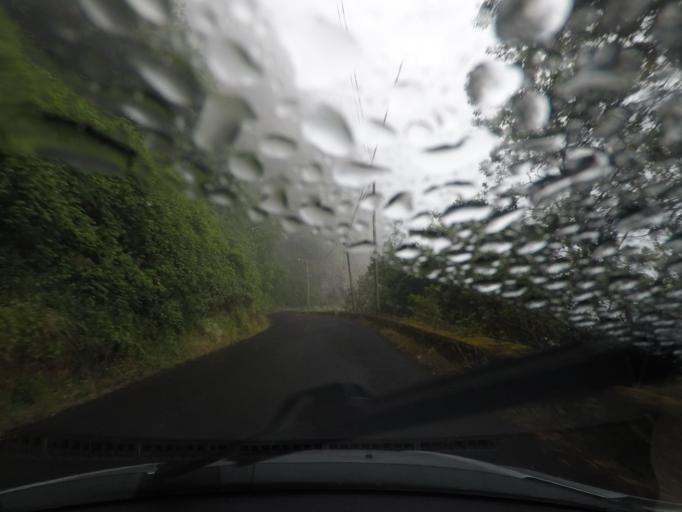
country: PT
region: Madeira
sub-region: Santana
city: Santana
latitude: 32.7565
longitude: -16.8700
